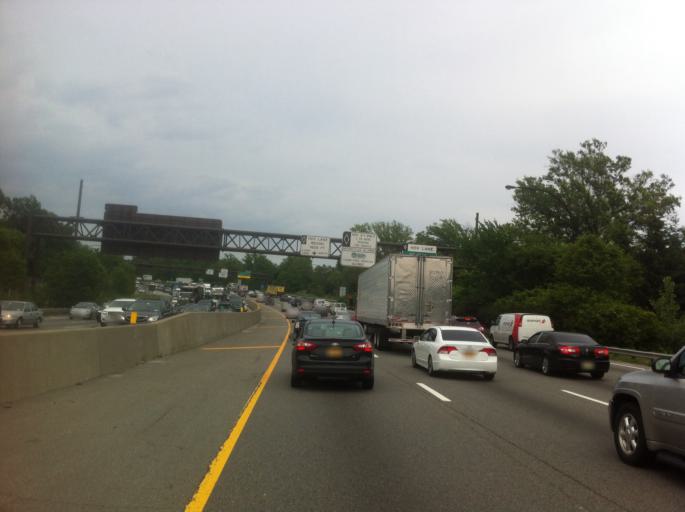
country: US
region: New York
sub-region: Nassau County
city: Lake Success
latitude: 40.7643
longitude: -73.7218
